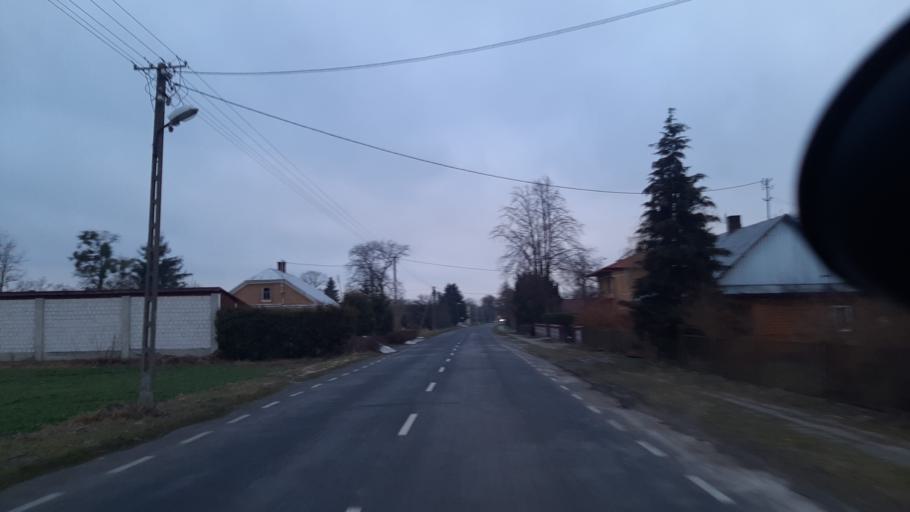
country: PL
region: Lublin Voivodeship
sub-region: Powiat parczewski
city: Debowa Kloda
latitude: 51.6379
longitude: 23.0394
